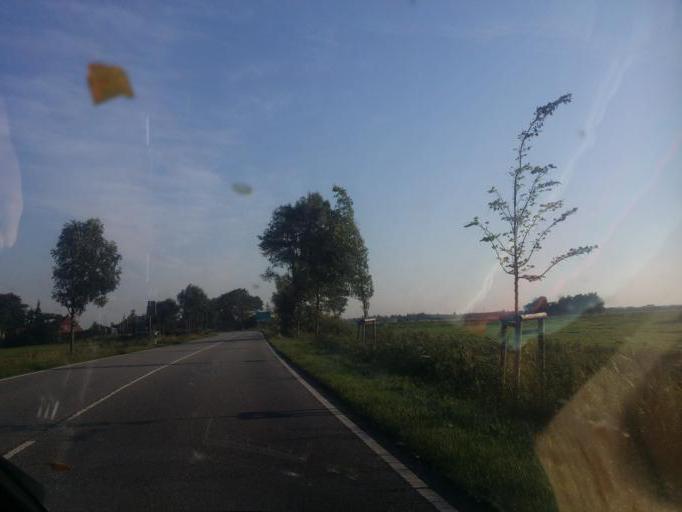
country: DE
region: Schleswig-Holstein
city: Suderlugum
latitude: 54.9018
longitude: 8.9105
